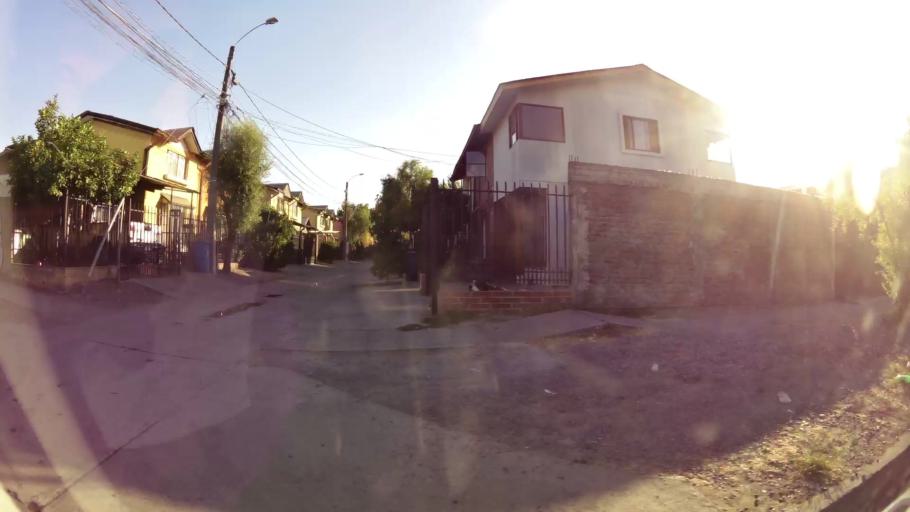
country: CL
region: Maule
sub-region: Provincia de Talca
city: Talca
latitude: -35.4476
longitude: -71.6802
